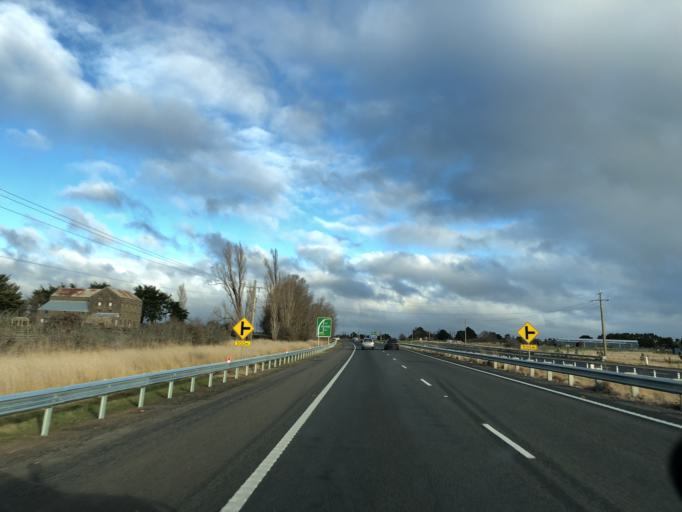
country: AU
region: Victoria
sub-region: Mount Alexander
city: Castlemaine
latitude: -37.2158
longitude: 144.4147
